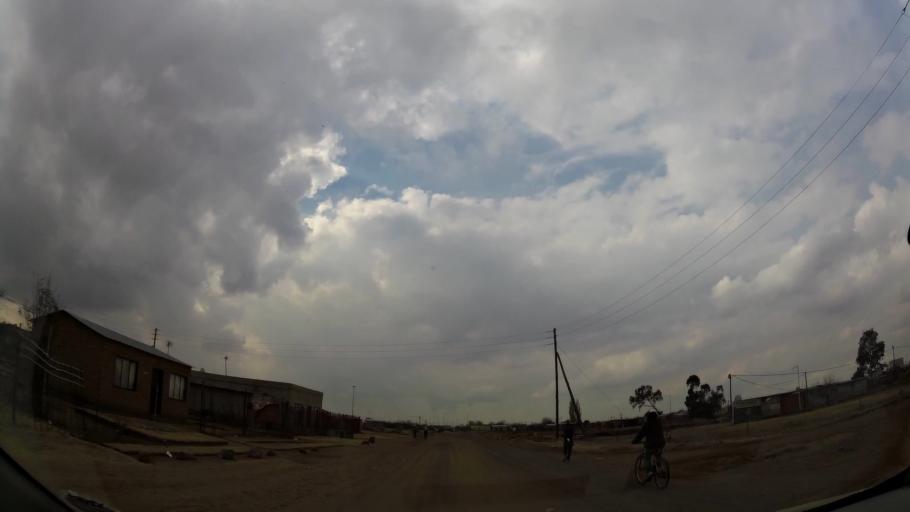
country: ZA
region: Orange Free State
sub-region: Fezile Dabi District Municipality
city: Sasolburg
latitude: -26.8622
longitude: 27.8805
